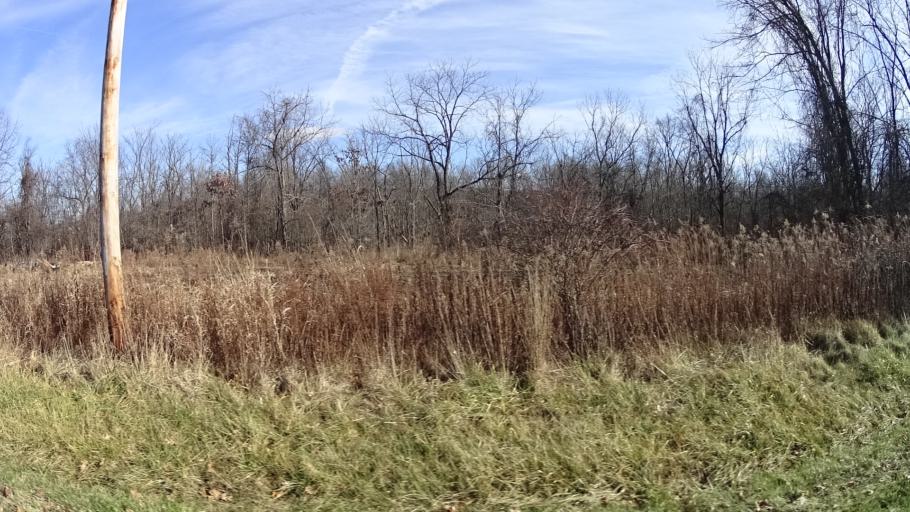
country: US
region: Ohio
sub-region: Lorain County
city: Wellington
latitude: 41.0776
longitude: -82.2591
